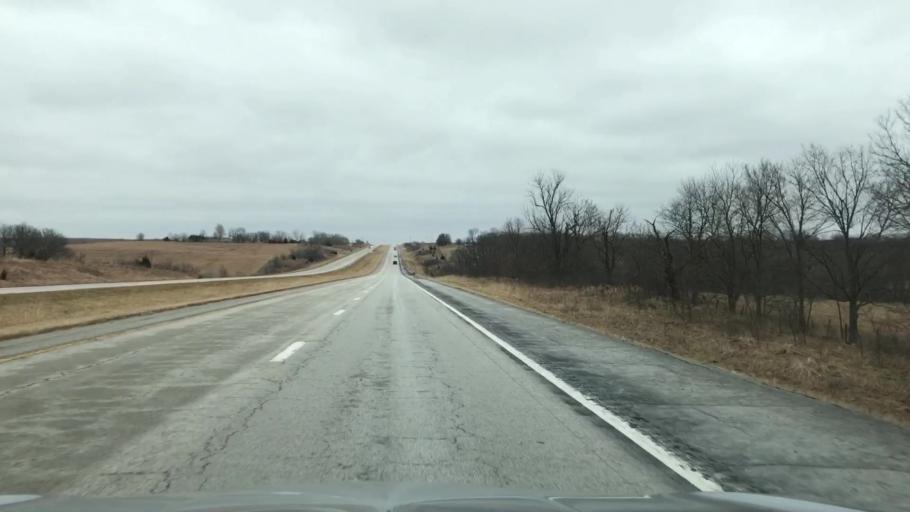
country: US
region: Missouri
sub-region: Caldwell County
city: Hamilton
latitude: 39.7499
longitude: -94.1019
